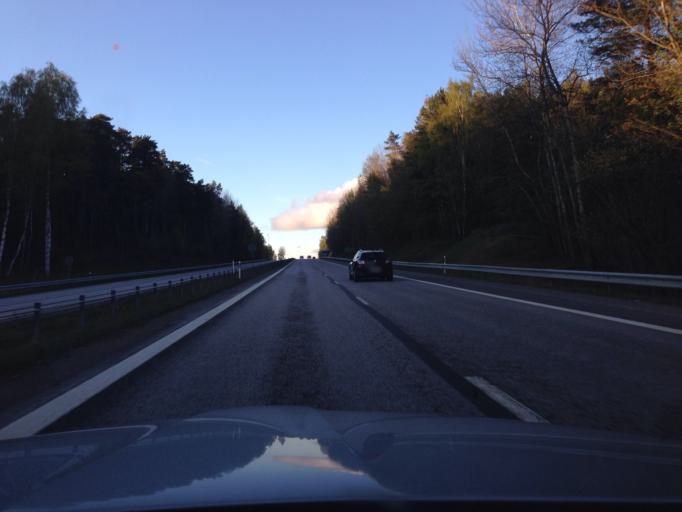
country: SE
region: Soedermanland
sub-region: Nykopings Kommun
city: Nykoping
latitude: 58.7592
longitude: 16.9864
